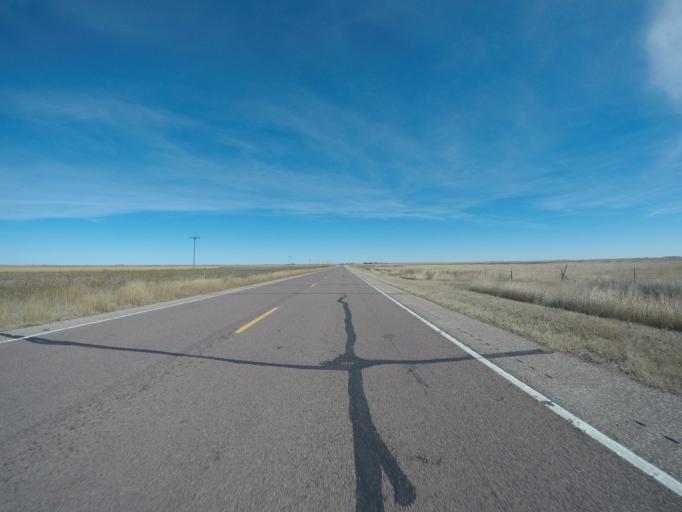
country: US
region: Colorado
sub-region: Kit Carson County
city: Burlington
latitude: 39.6575
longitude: -102.5630
